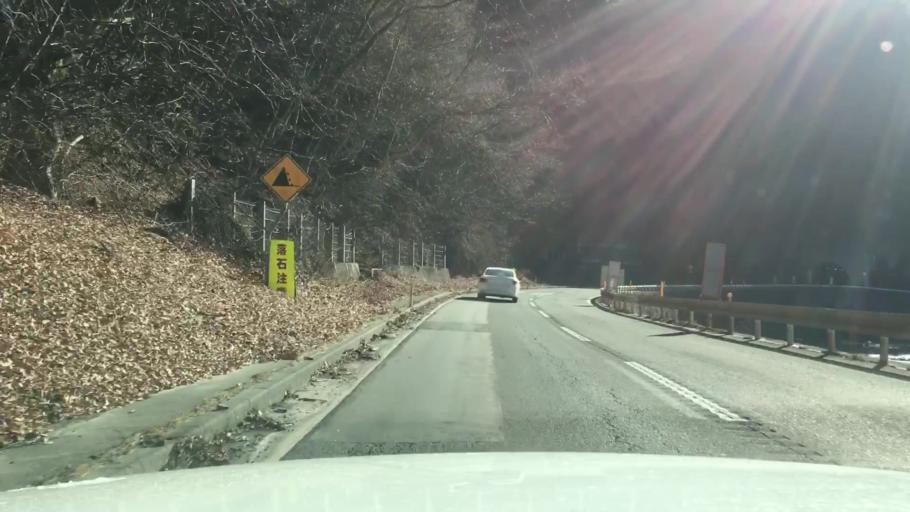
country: JP
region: Iwate
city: Miyako
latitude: 39.6009
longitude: 141.7118
